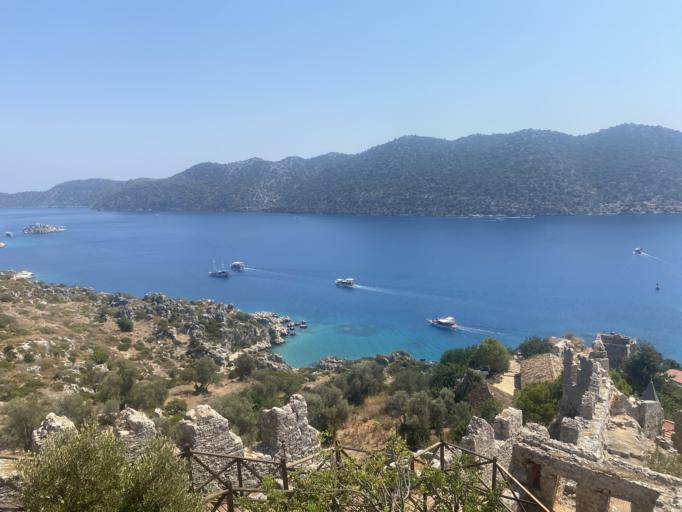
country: TR
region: Antalya
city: Demre
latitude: 36.1914
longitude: 29.8622
